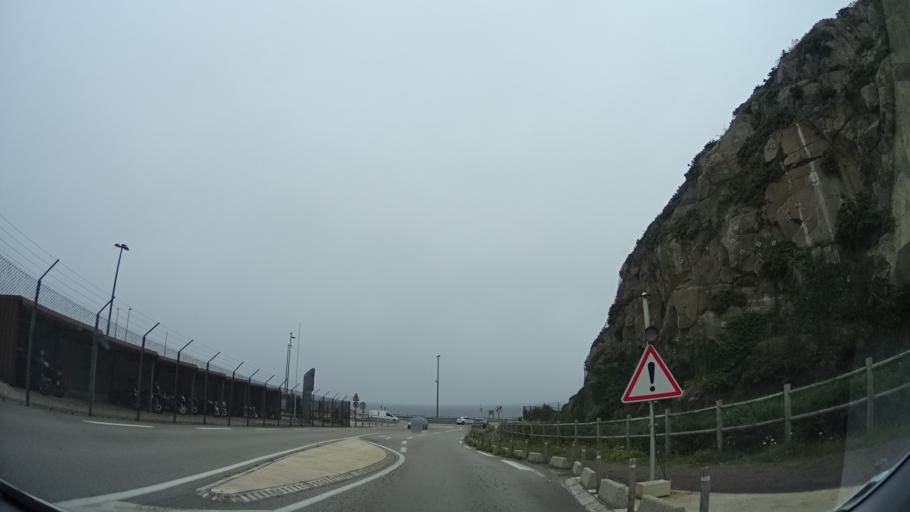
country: FR
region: Lower Normandy
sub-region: Departement de la Manche
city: Flamanville
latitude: 49.5442
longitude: -1.8742
